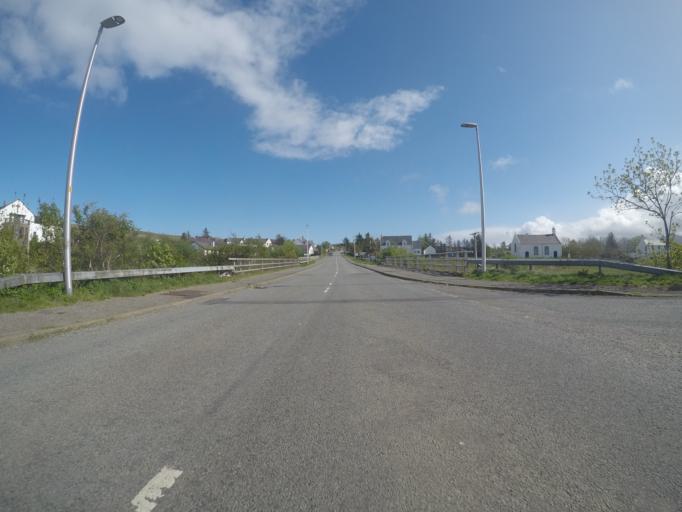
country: GB
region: Scotland
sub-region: Highland
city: Portree
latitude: 57.6267
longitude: -6.2074
